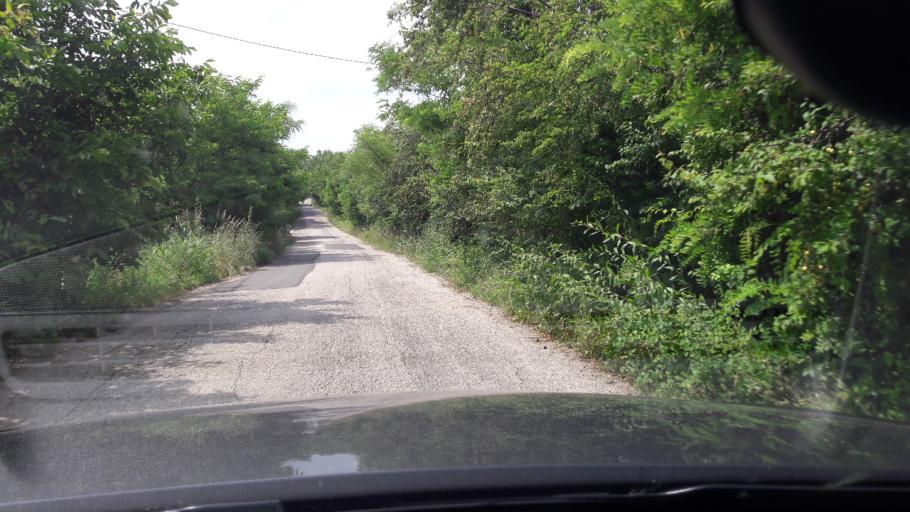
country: RS
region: Central Serbia
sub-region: Belgrade
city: Sopot
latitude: 44.6086
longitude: 20.5990
